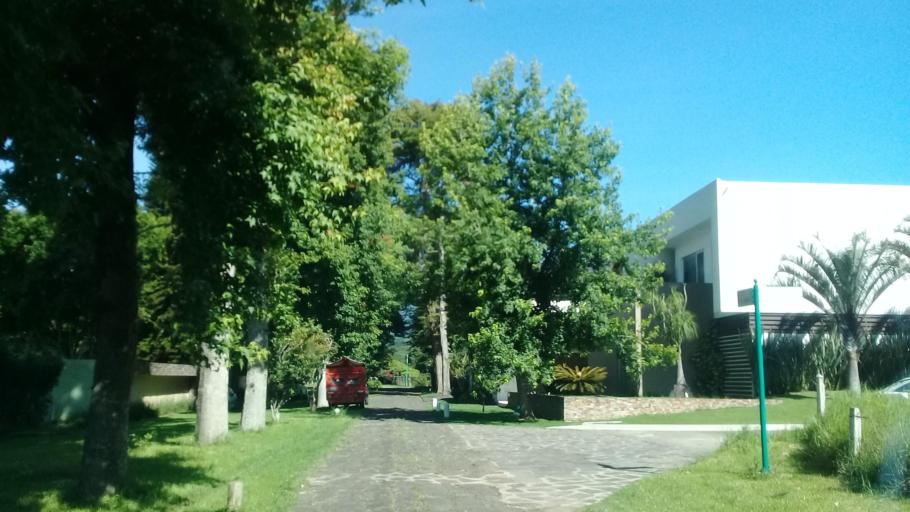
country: MX
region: Veracruz
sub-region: Tlalnelhuayocan
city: Guadalupe Victoria
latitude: 19.5339
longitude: -96.9484
